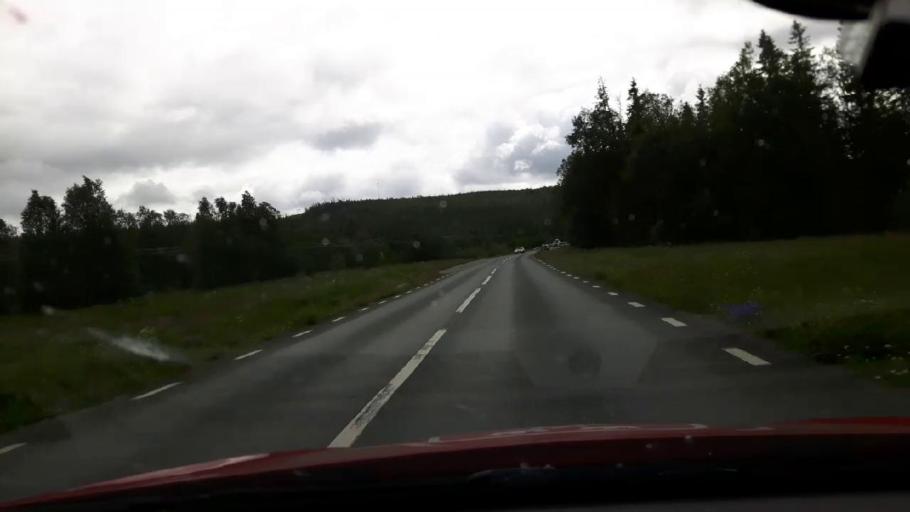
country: SE
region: Jaemtland
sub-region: Are Kommun
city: Are
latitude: 63.3619
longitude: 12.6957
